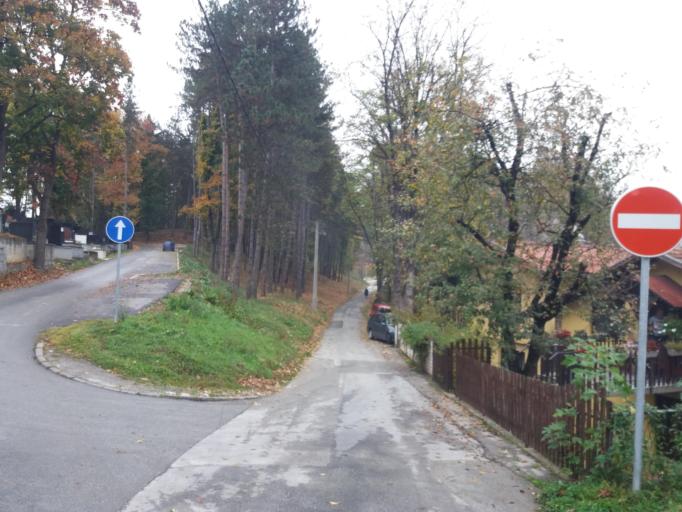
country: RS
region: Central Serbia
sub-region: Zlatiborski Okrug
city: Uzice
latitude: 43.8500
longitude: 19.8507
